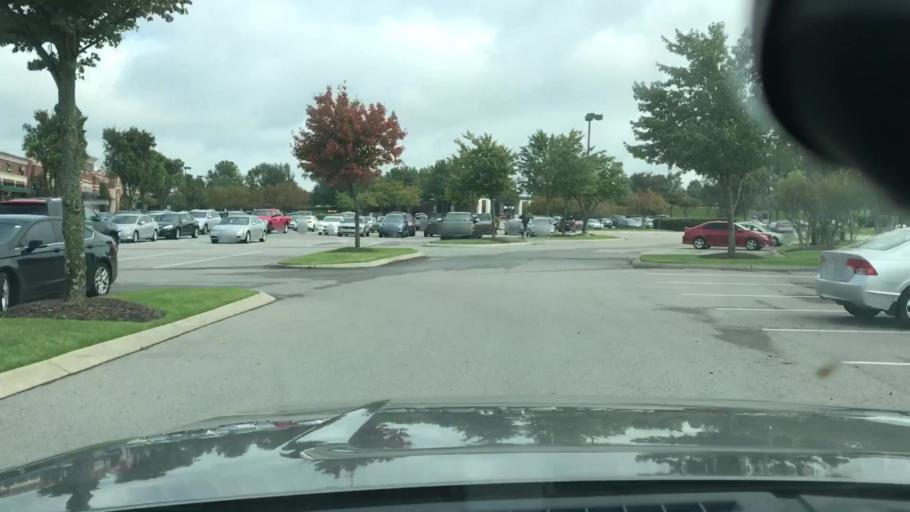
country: US
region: Tennessee
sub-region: Williamson County
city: Franklin
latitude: 35.9479
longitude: -86.8229
